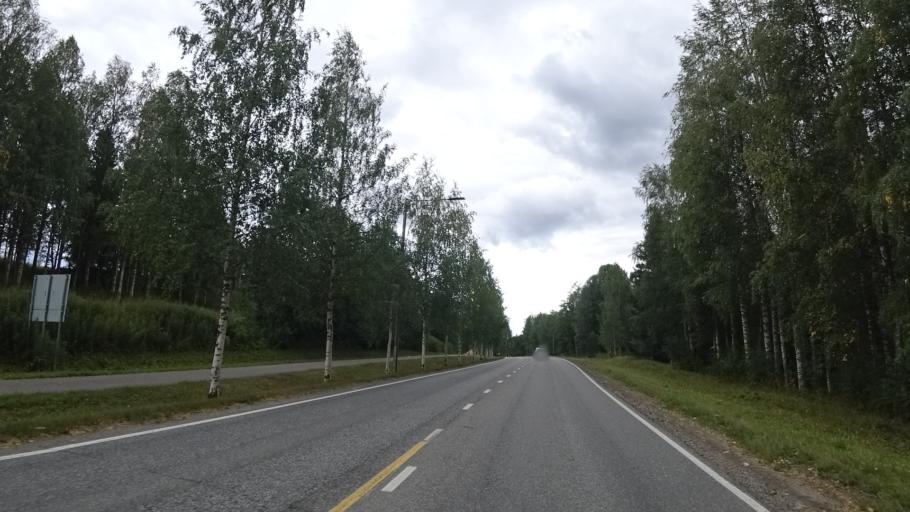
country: FI
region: North Karelia
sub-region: Joensuu
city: Ilomantsi
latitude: 62.6606
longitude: 30.9343
